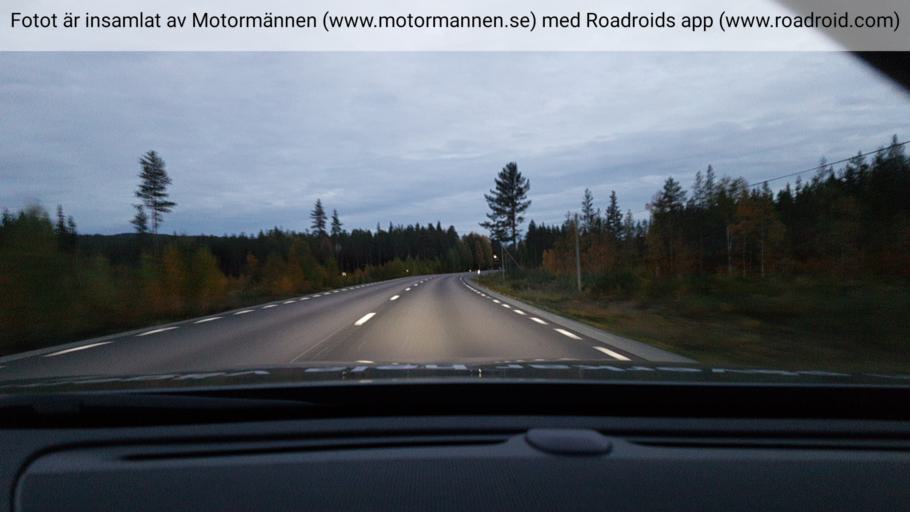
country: SE
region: Norrbotten
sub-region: Alvsbyns Kommun
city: AElvsbyn
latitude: 65.7069
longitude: 20.9946
